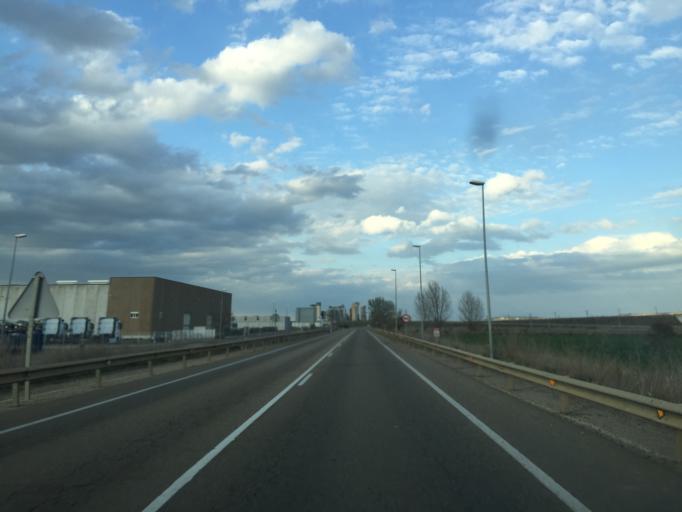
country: ES
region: Castille and Leon
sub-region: Provincia de Palencia
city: Venta de Banos
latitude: 41.9318
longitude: -4.4817
